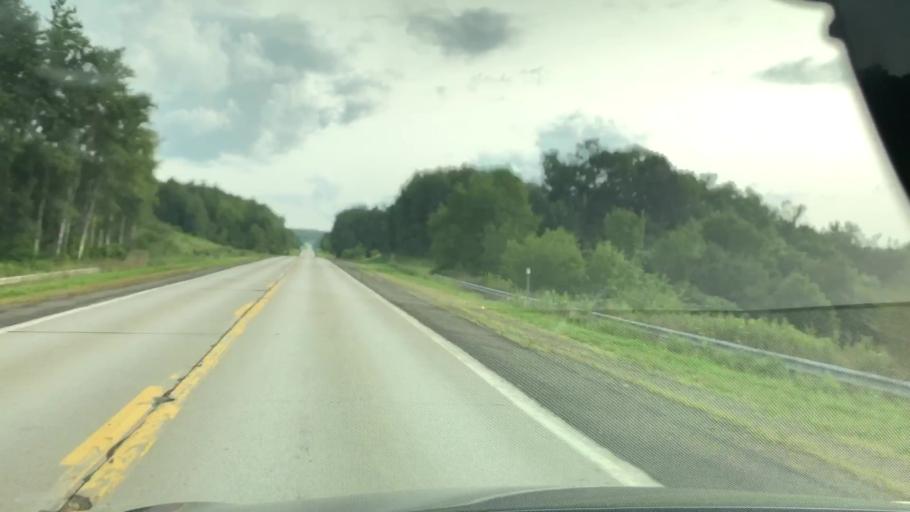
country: US
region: Pennsylvania
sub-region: Erie County
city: Union City
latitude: 41.9792
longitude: -79.8402
